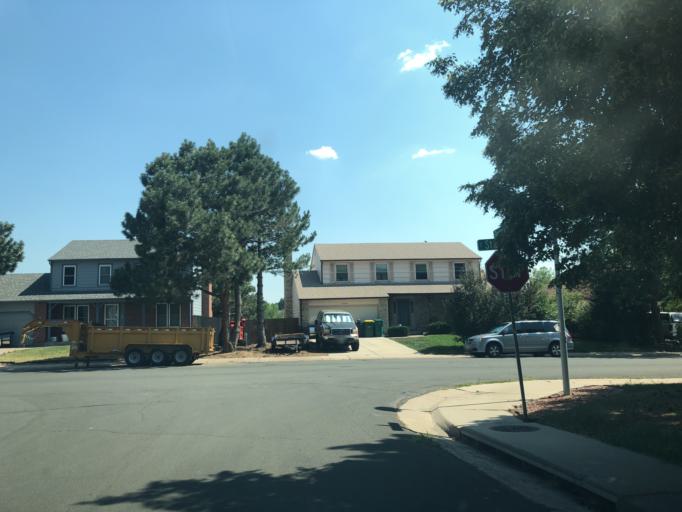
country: US
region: Colorado
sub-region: Arapahoe County
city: Dove Valley
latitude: 39.6355
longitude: -104.7682
